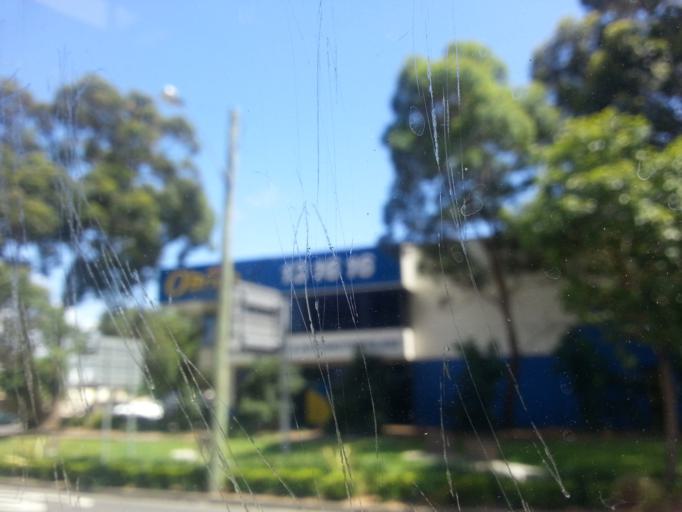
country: AU
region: New South Wales
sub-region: City of Sydney
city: Alexandria
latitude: -33.9016
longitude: 151.2006
